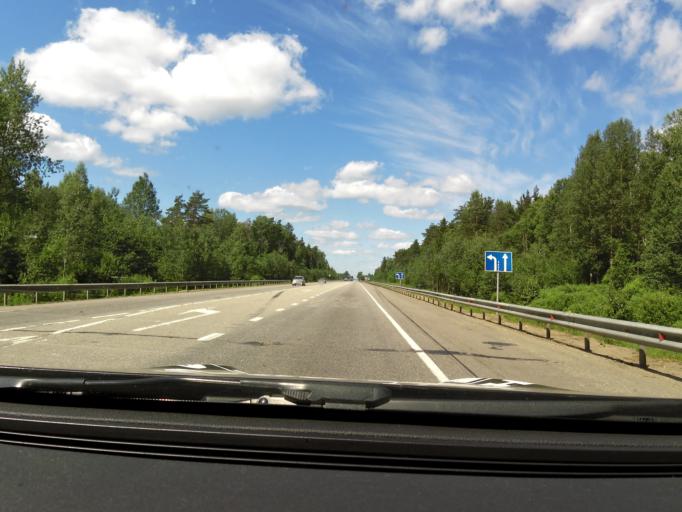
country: RU
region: Tverskaya
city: Kuzhenkino
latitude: 57.8045
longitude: 33.8585
